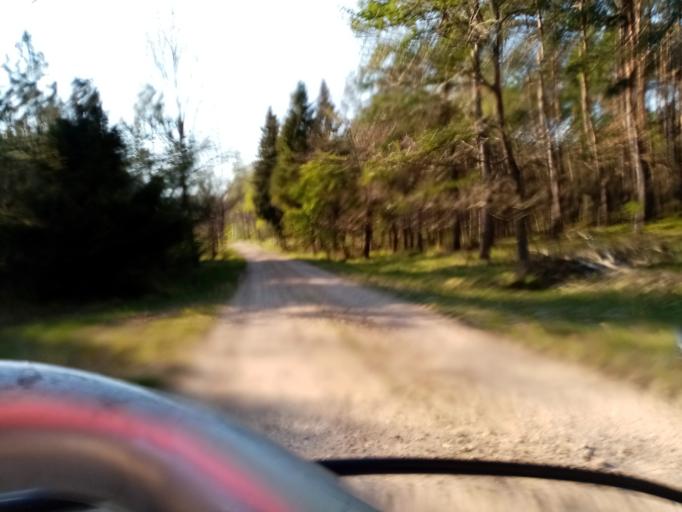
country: PL
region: Kujawsko-Pomorskie
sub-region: Powiat brodnicki
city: Gorzno
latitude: 53.1688
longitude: 19.6717
